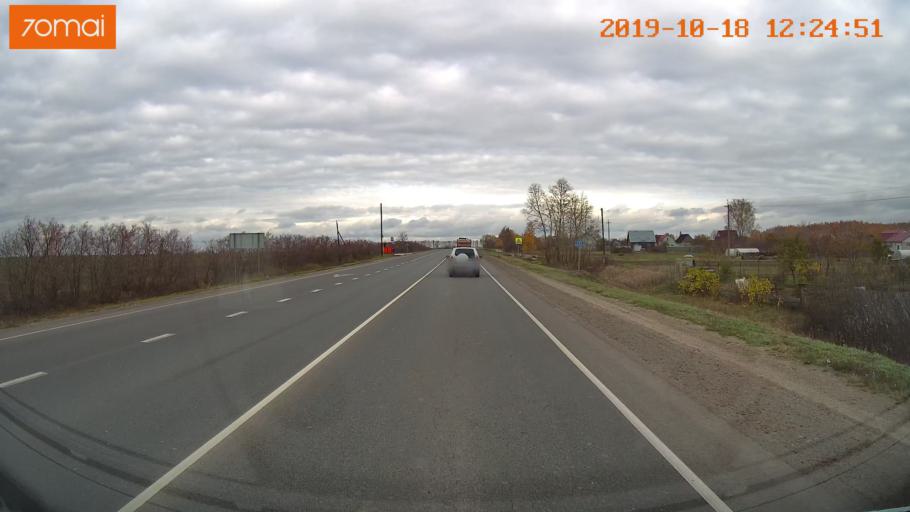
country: RU
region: Rjazan
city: Rybnoye
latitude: 54.5432
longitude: 39.5155
